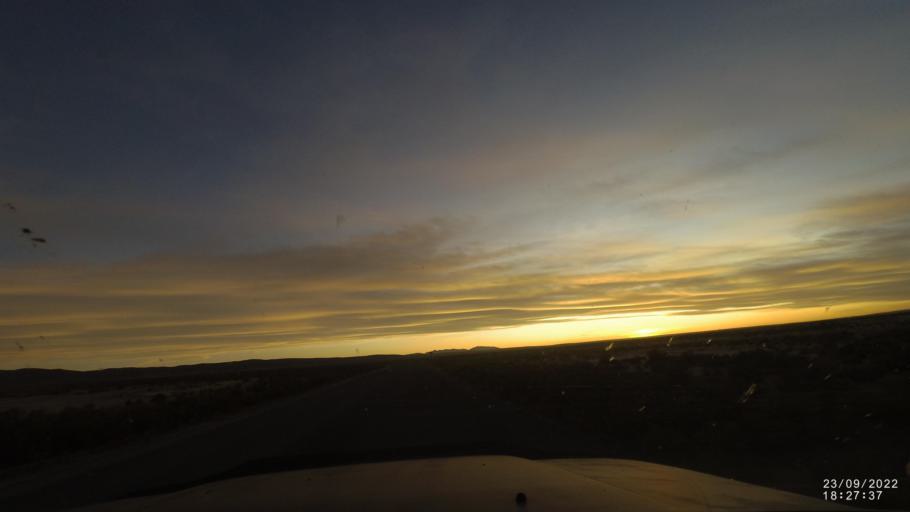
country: BO
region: Oruro
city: Challapata
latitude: -19.3298
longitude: -67.1699
